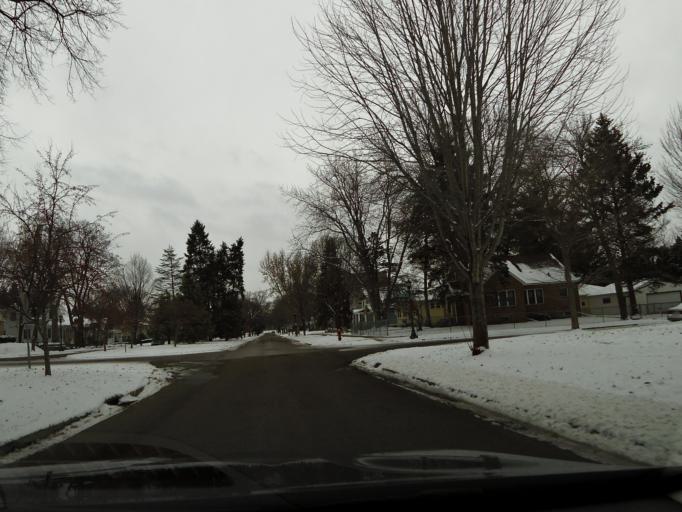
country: US
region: Minnesota
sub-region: Dakota County
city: Mendota Heights
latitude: 44.9275
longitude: -93.1501
